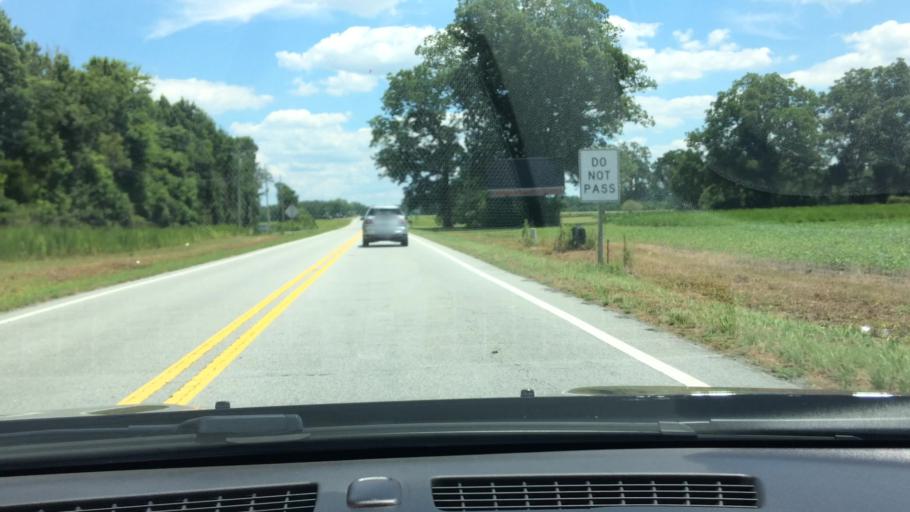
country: US
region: North Carolina
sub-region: Pitt County
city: Summerfield
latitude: 35.6302
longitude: -77.4376
